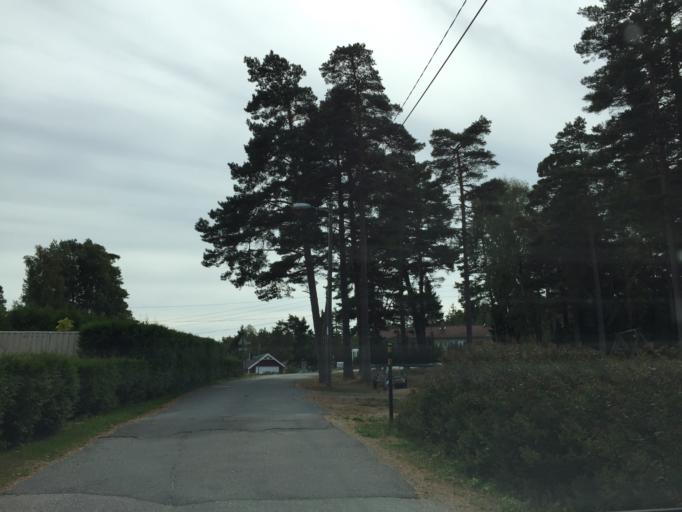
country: NO
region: Ostfold
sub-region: Fredrikstad
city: Fredrikstad
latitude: 59.0976
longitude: 10.9372
